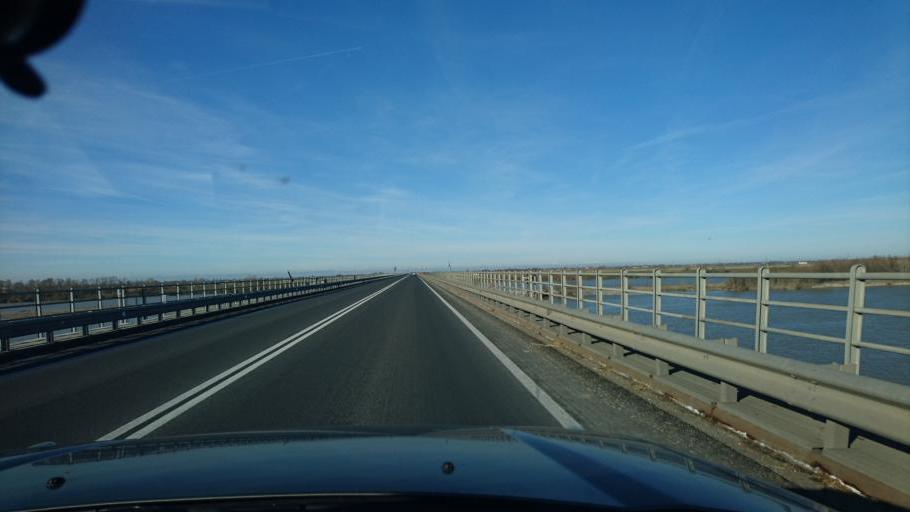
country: IT
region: Veneto
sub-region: Provincia di Rovigo
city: Bottrighe
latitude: 45.0183
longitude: 12.0998
